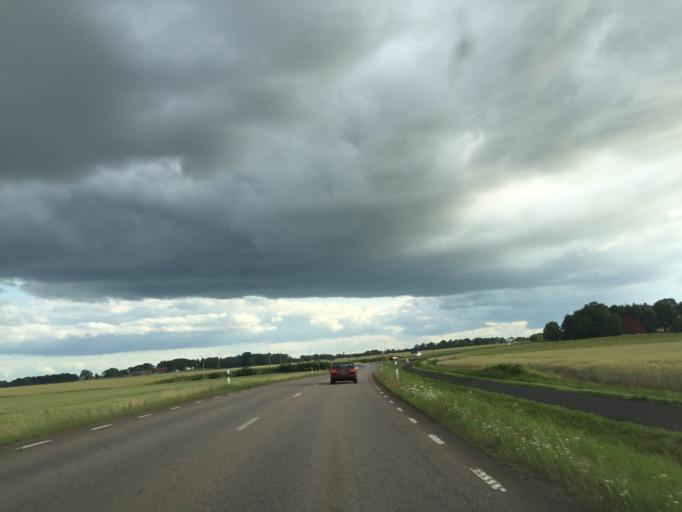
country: SE
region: OEstergoetland
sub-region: Vadstena Kommun
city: Vadstena
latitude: 58.4593
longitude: 14.9251
